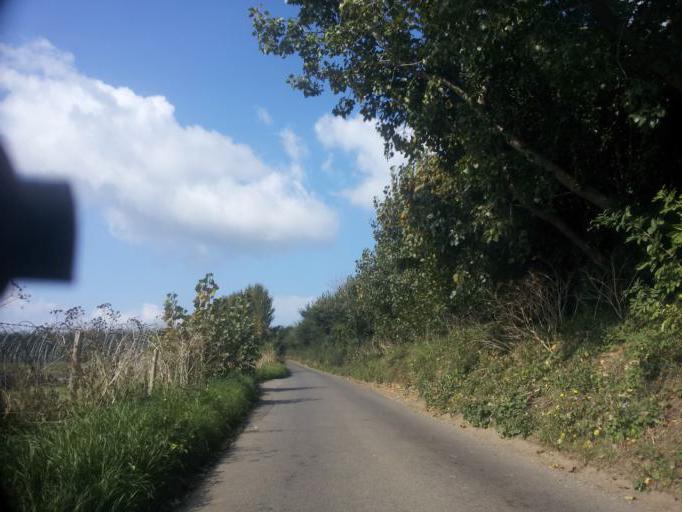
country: GB
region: England
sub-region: Kent
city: Strood
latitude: 51.4168
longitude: 0.5016
